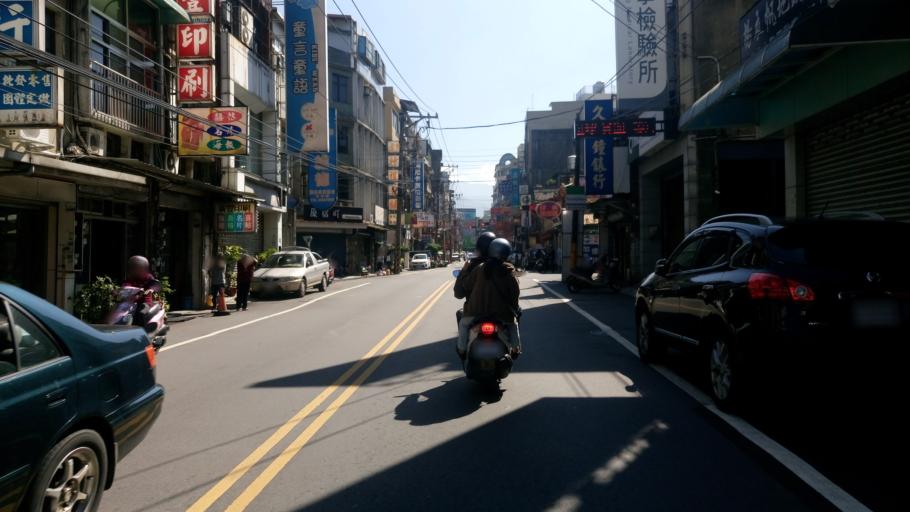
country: TW
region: Taiwan
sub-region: Hsinchu
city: Zhubei
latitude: 24.7387
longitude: 121.0867
